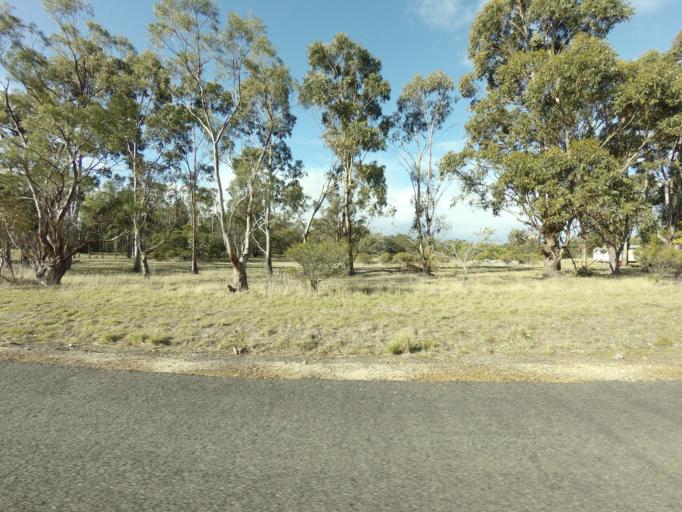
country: AU
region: Tasmania
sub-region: Sorell
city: Sorell
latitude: -42.3064
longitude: 147.9903
